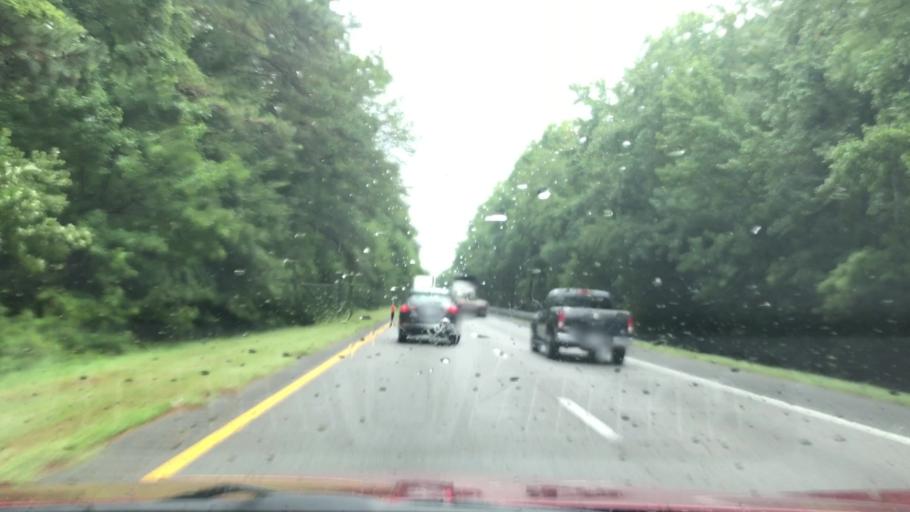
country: US
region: South Carolina
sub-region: Dorchester County
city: Ridgeville
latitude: 33.1020
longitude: -80.2453
